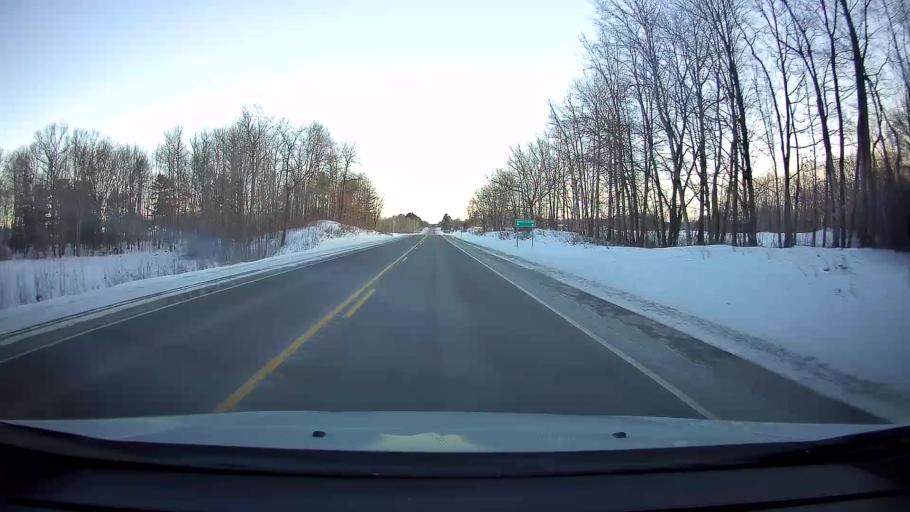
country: US
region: Wisconsin
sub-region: Washburn County
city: Shell Lake
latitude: 45.6882
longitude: -91.9742
